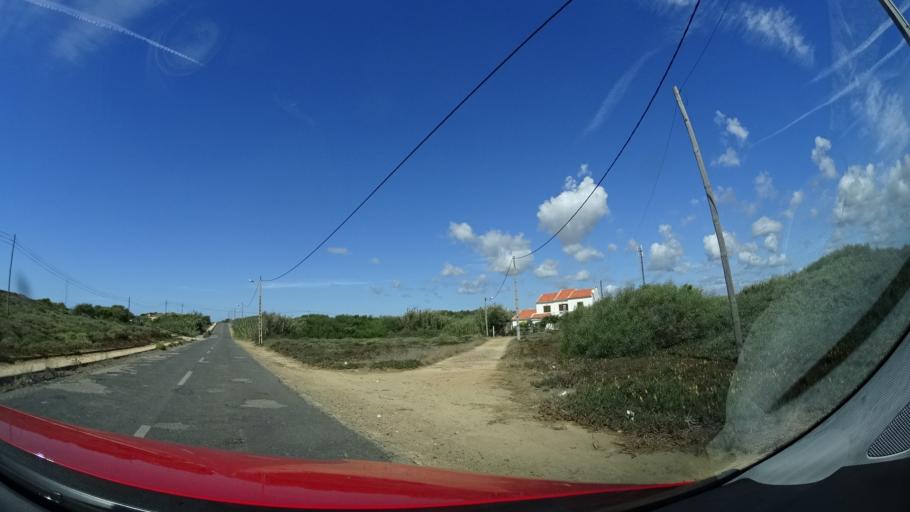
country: PT
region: Beja
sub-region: Odemira
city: Sao Teotonio
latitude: 37.5305
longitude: -8.7843
